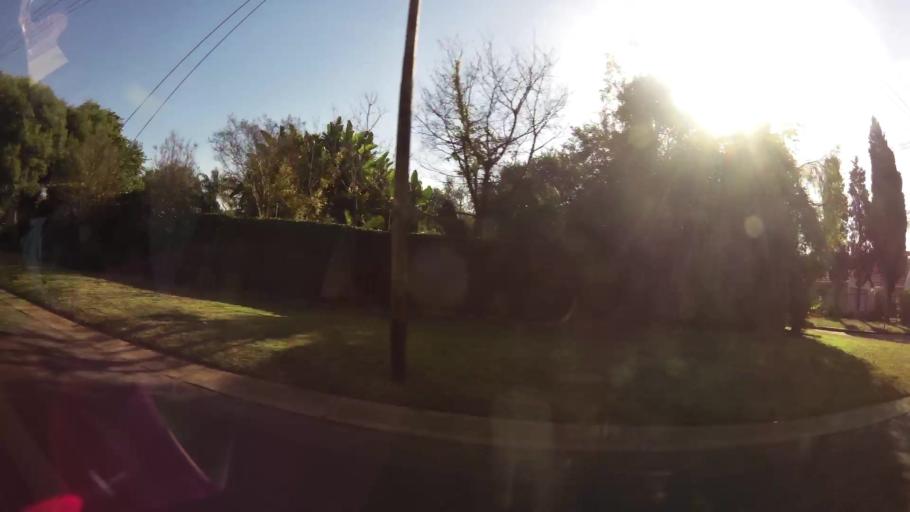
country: ZA
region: Gauteng
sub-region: City of Tshwane Metropolitan Municipality
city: Pretoria
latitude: -25.7223
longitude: 28.2612
